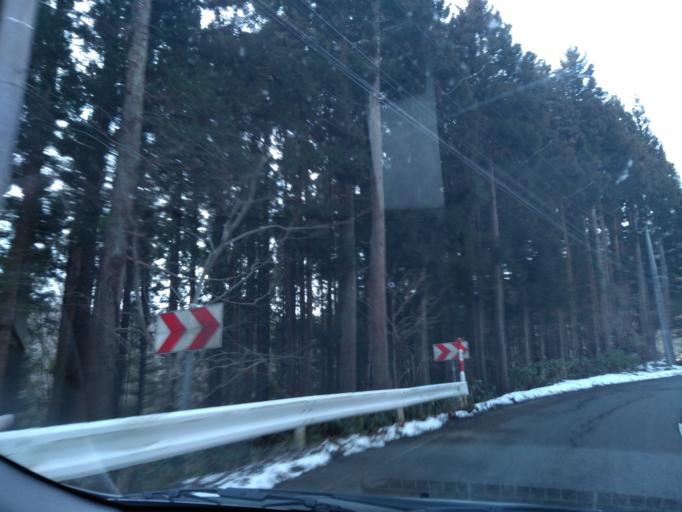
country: JP
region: Iwate
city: Kitakami
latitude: 39.2397
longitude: 140.9778
